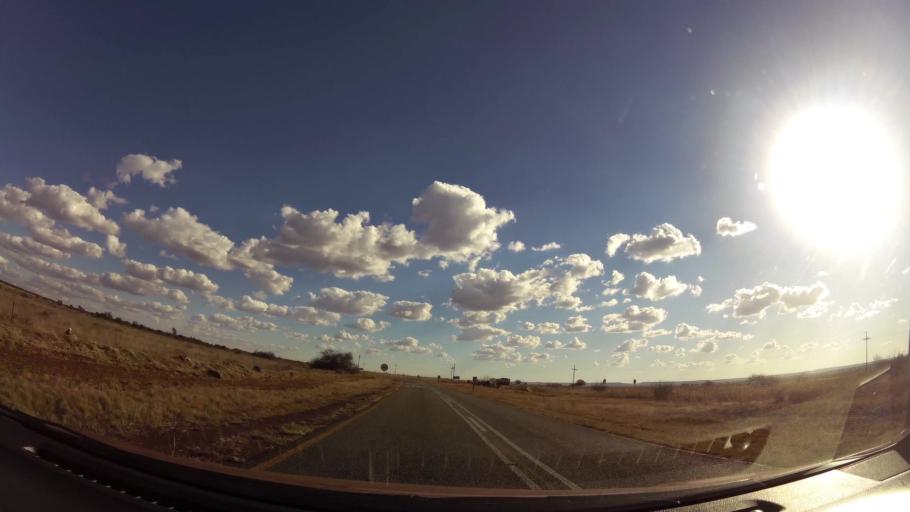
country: ZA
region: Gauteng
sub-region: West Rand District Municipality
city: Carletonville
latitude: -26.4126
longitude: 27.2376
